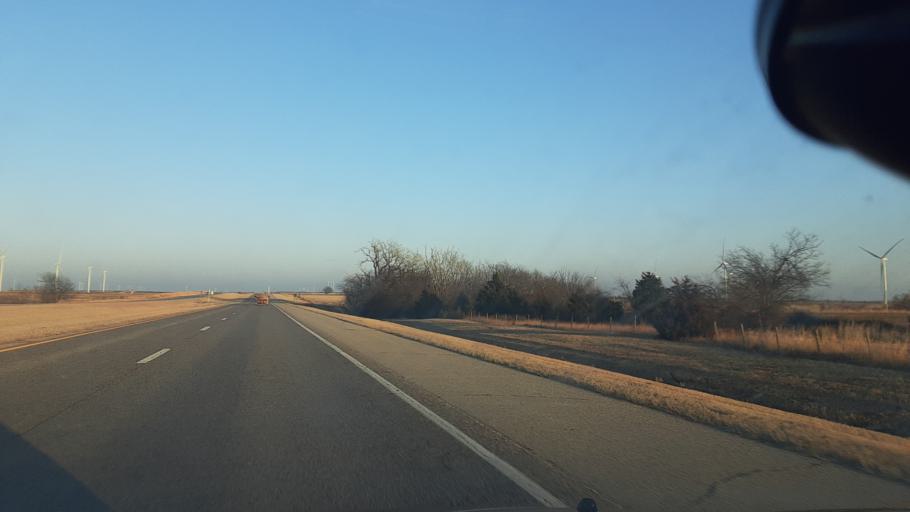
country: US
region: Oklahoma
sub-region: Noble County
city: Perry
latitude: 36.3976
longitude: -97.5170
